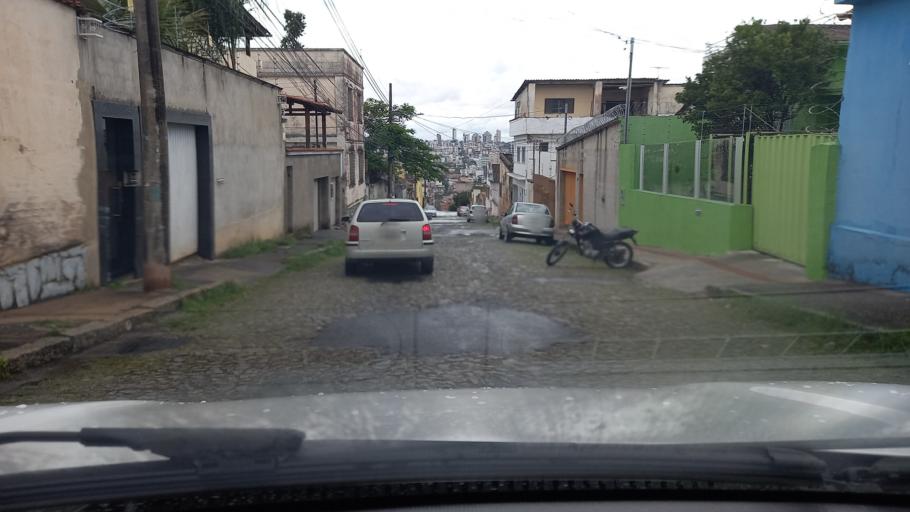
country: BR
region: Minas Gerais
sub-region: Belo Horizonte
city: Belo Horizonte
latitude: -19.9065
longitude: -43.9521
